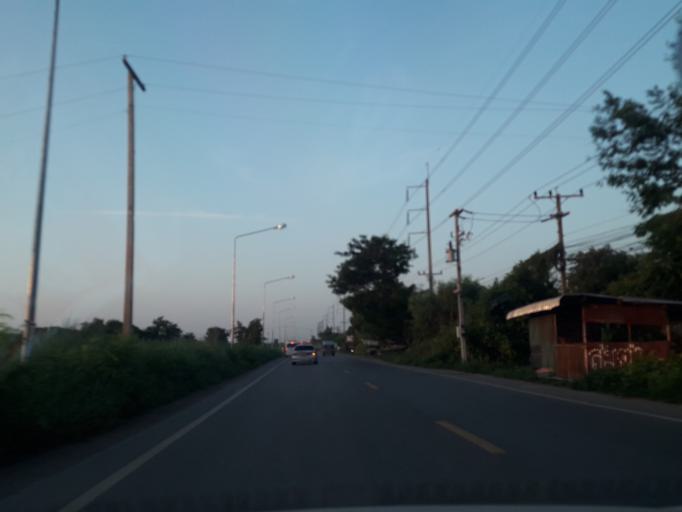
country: TH
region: Phra Nakhon Si Ayutthaya
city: Bang Pahan
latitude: 14.4748
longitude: 100.5522
